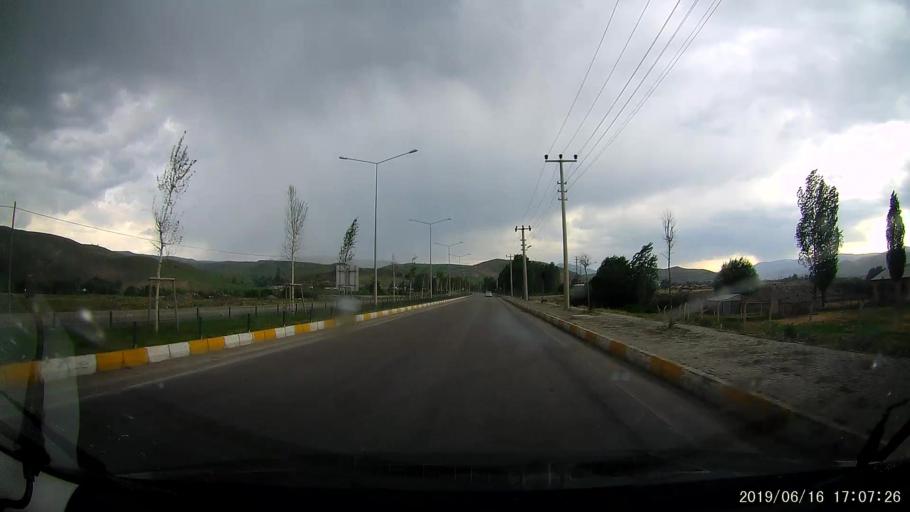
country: TR
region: Erzurum
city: Askale
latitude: 39.9177
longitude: 40.6761
